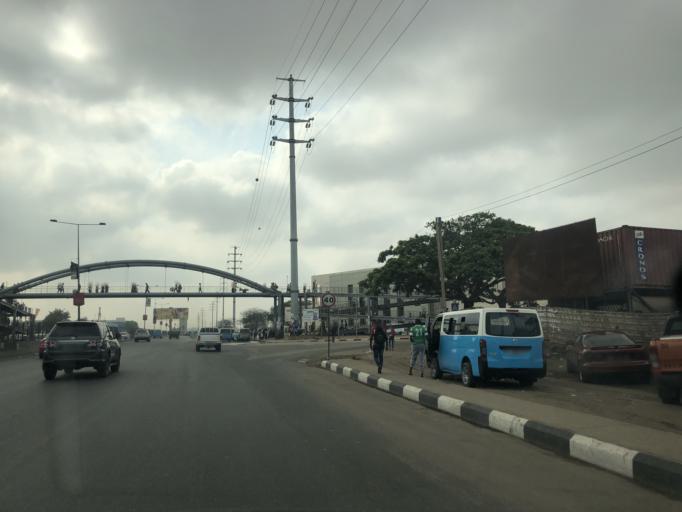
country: AO
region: Luanda
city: Luanda
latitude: -8.8383
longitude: 13.2630
